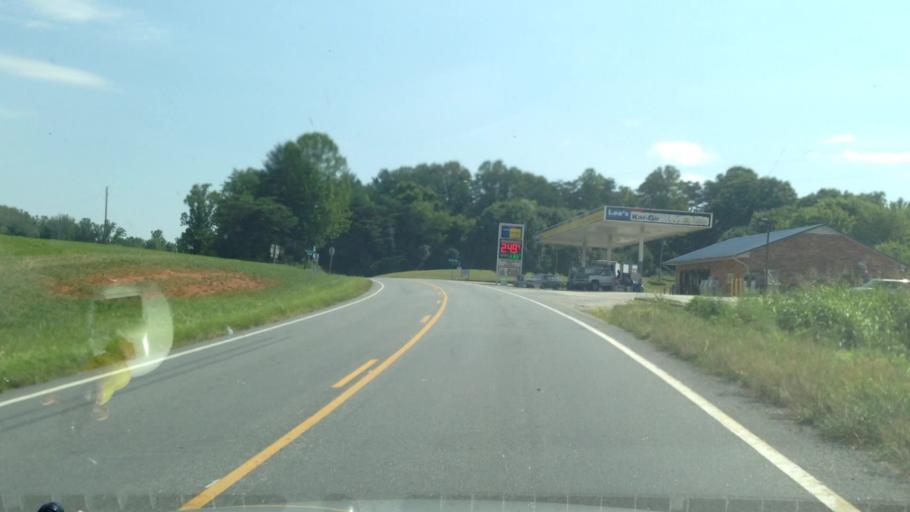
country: US
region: North Carolina
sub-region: Surry County
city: Flat Rock
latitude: 36.5597
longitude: -80.4689
